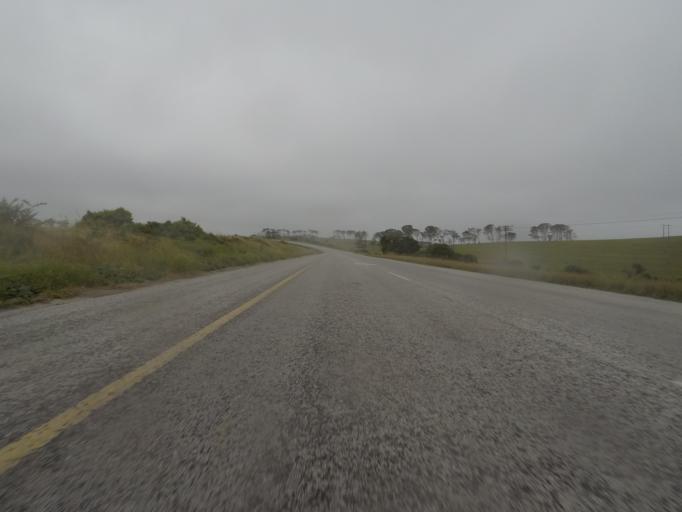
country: ZA
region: Eastern Cape
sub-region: Cacadu District Municipality
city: Grahamstown
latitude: -33.6434
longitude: 26.3418
